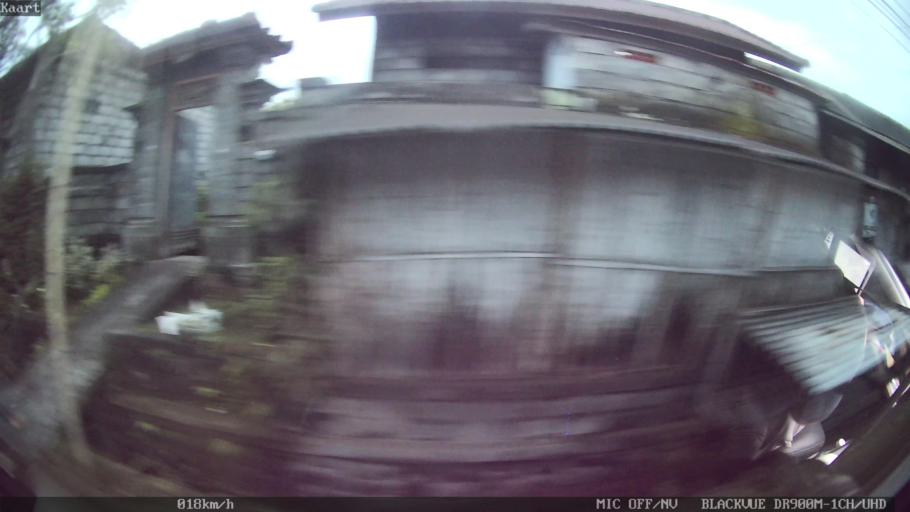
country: ID
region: Bali
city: Banjar Pasekan
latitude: -8.6165
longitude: 115.2753
